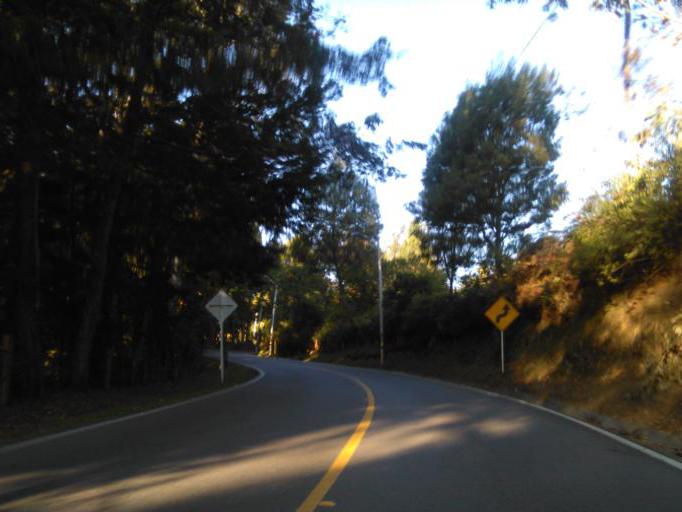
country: CO
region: Antioquia
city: La Ceja
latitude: 6.0079
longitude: -75.4053
